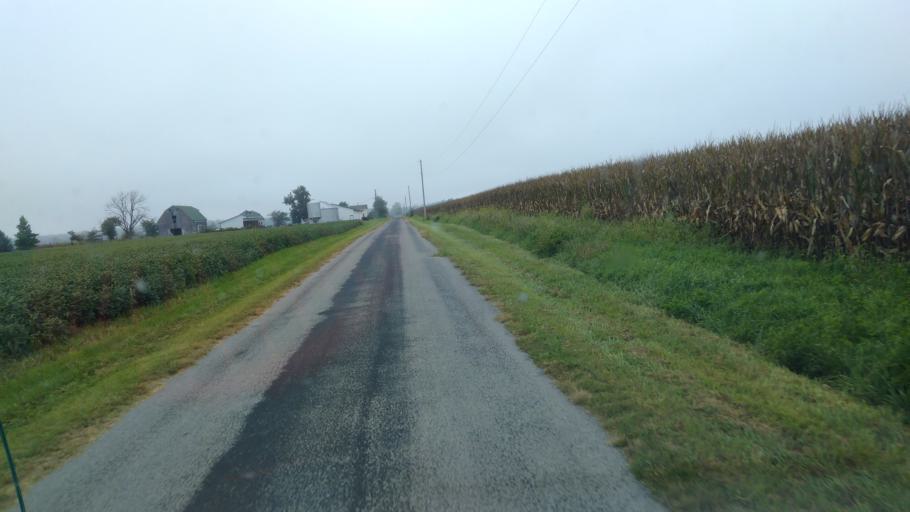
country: US
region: Ohio
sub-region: Hardin County
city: Kenton
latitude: 40.5166
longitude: -83.6002
